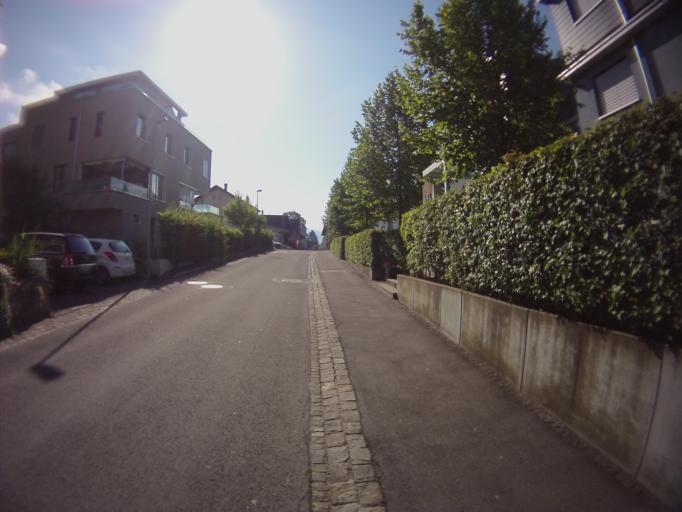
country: CH
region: Zug
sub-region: Zug
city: Unterageri
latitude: 47.1400
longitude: 8.5745
